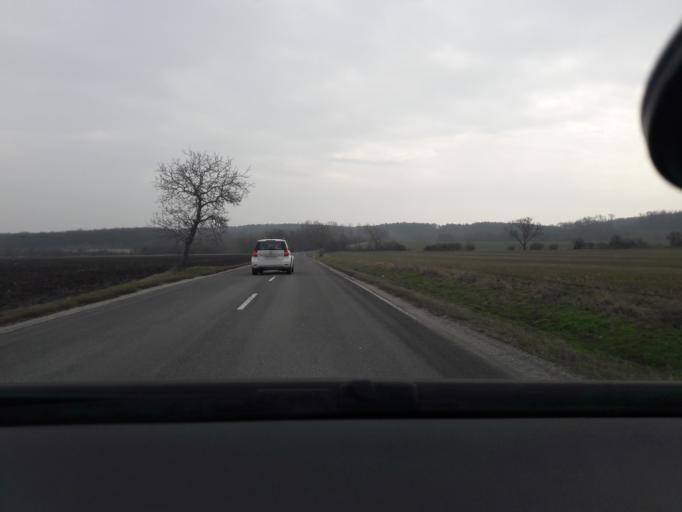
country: SK
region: Trnavsky
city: Smolenice
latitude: 48.4878
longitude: 17.4248
